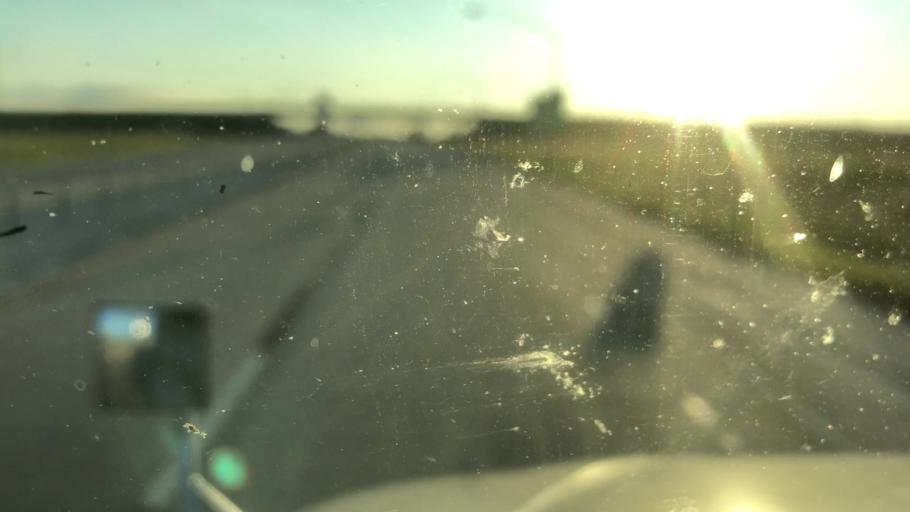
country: US
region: Oklahoma
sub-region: Noble County
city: Perry
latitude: 36.3837
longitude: -97.0645
